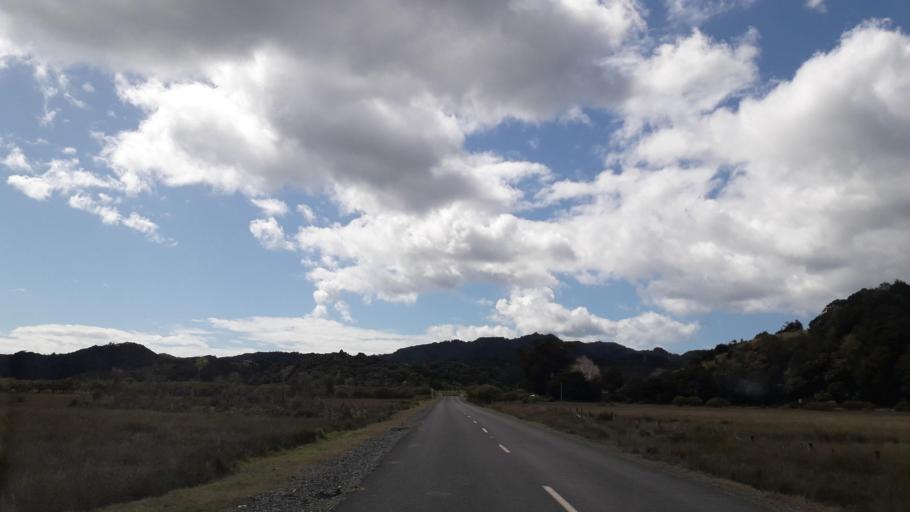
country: NZ
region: Northland
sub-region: Far North District
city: Paihia
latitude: -35.3383
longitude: 174.2284
